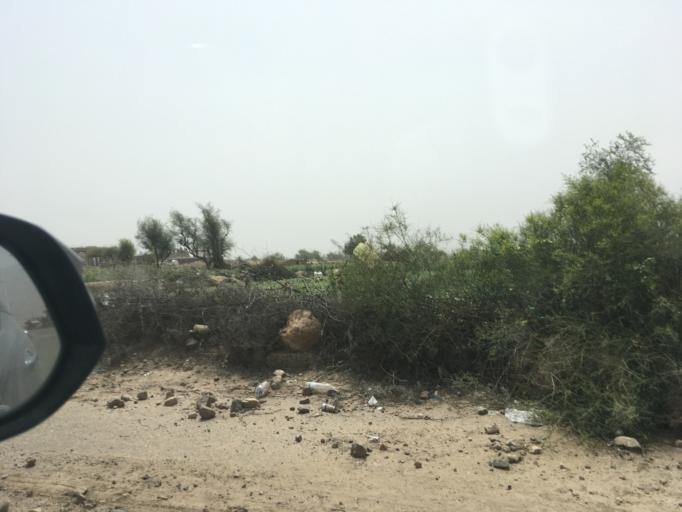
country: YE
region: Ad Dali'
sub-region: Qa'atabah
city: Qa`tabah
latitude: 13.8204
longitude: 44.7157
